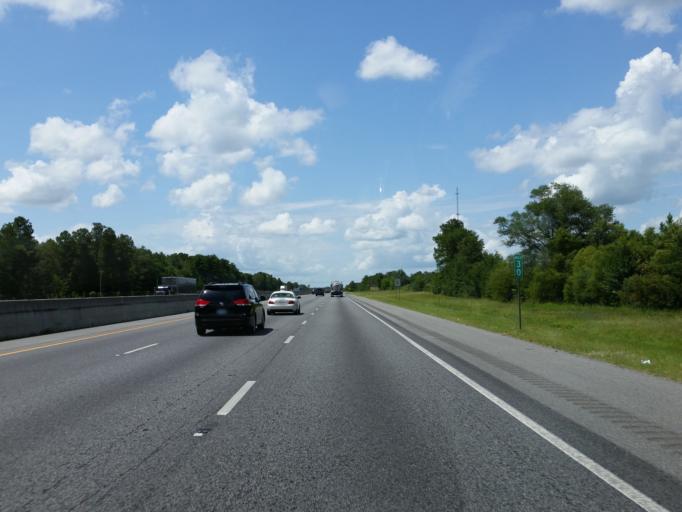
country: US
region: Georgia
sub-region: Lowndes County
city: Hahira
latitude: 31.0104
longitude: -83.3931
